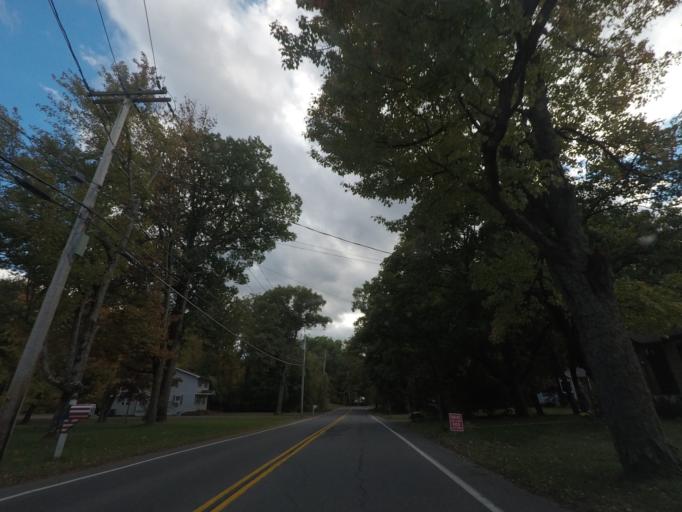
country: US
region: New York
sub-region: Albany County
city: Colonie
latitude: 42.7380
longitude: -73.8395
